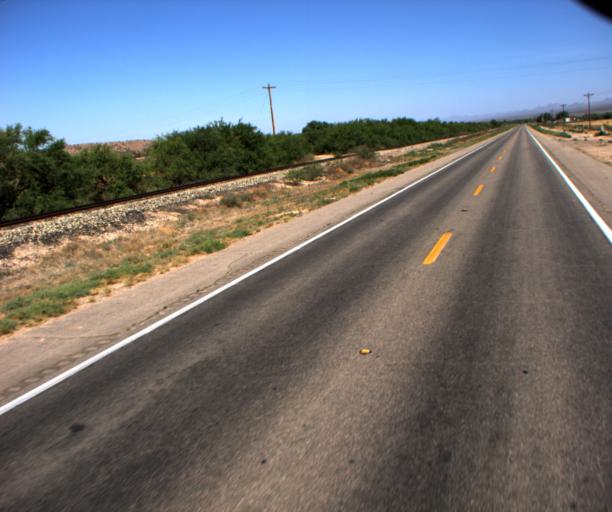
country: US
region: Arizona
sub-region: Graham County
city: Pima
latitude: 33.0120
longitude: -109.9499
